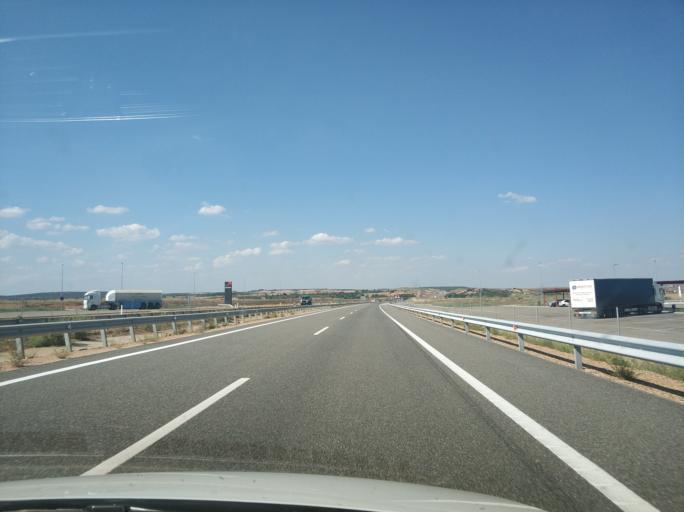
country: ES
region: Castille and Leon
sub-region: Provincia de Zamora
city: Granja de Moreruela
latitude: 41.7981
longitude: -5.7562
